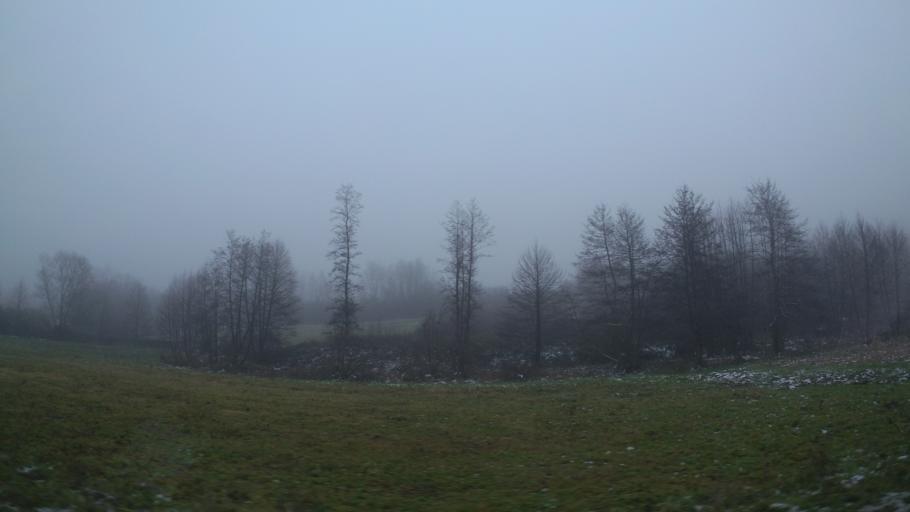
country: HR
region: Sisacko-Moslavacka
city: Glina
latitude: 45.3070
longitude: 16.0061
